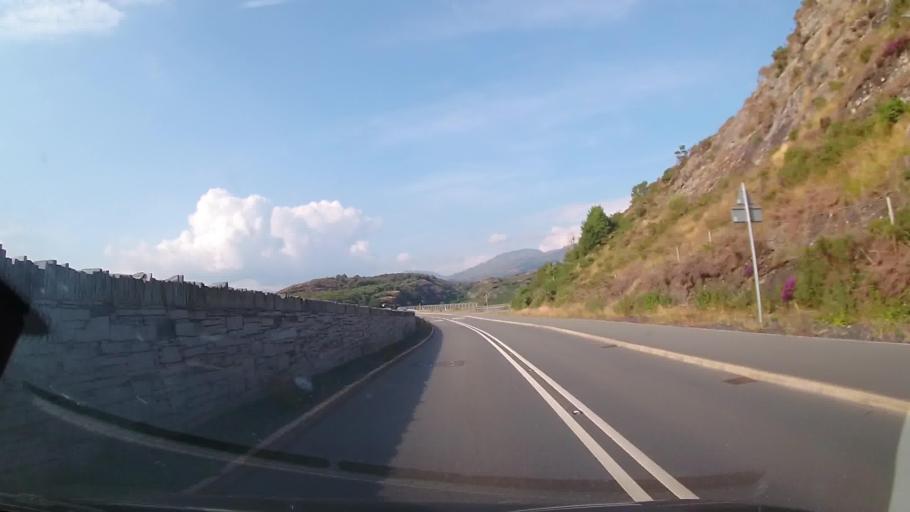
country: GB
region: Wales
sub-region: Gwynedd
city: Penrhyndeudraeth
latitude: 52.9219
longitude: -4.0562
